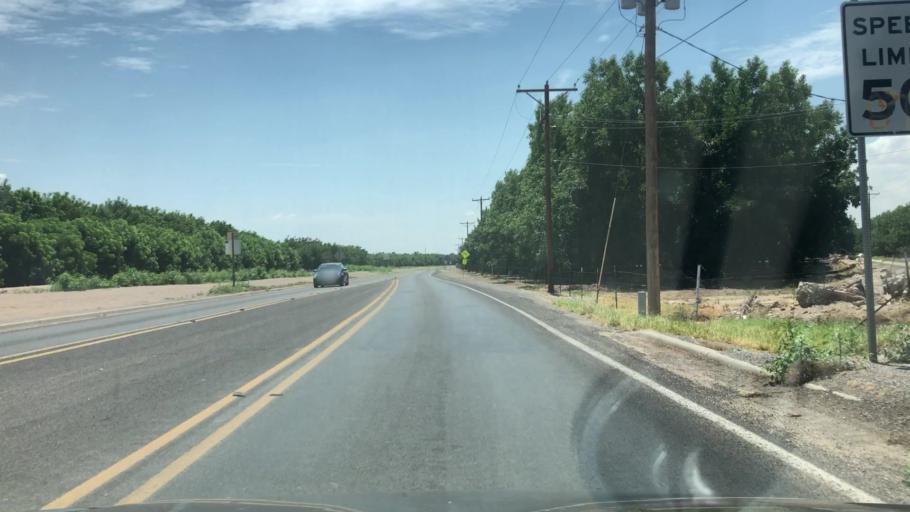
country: US
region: New Mexico
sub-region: Dona Ana County
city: La Union
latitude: 31.9959
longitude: -106.6544
